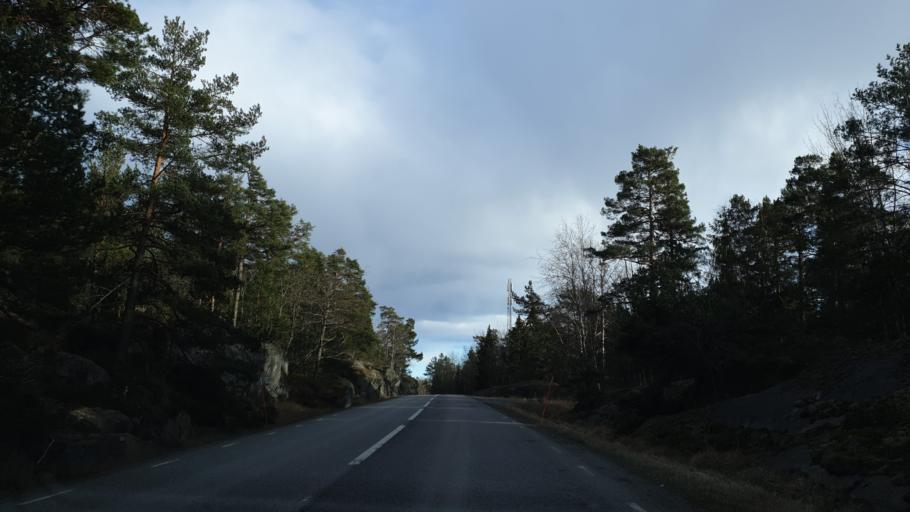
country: SE
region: Stockholm
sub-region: Varmdo Kommun
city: Holo
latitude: 59.3308
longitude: 18.7198
